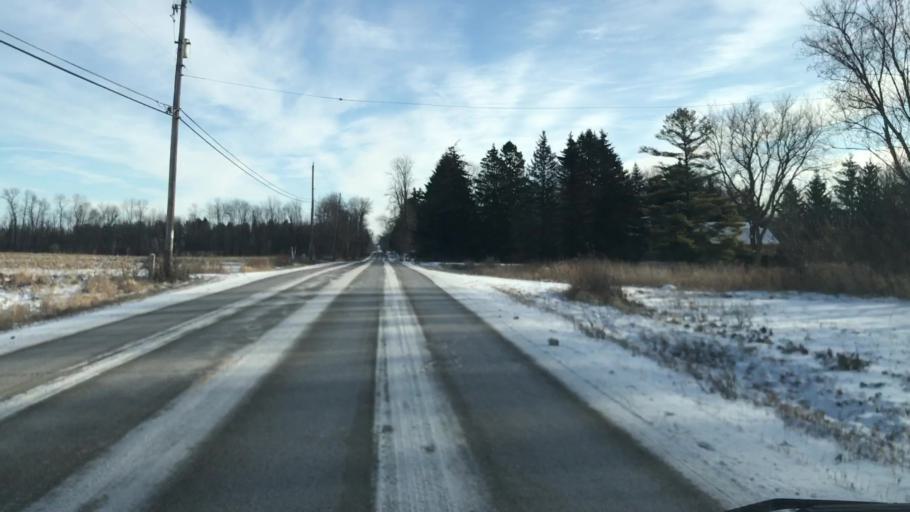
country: US
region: Wisconsin
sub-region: Waukesha County
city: Lannon
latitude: 43.1700
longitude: -88.1544
